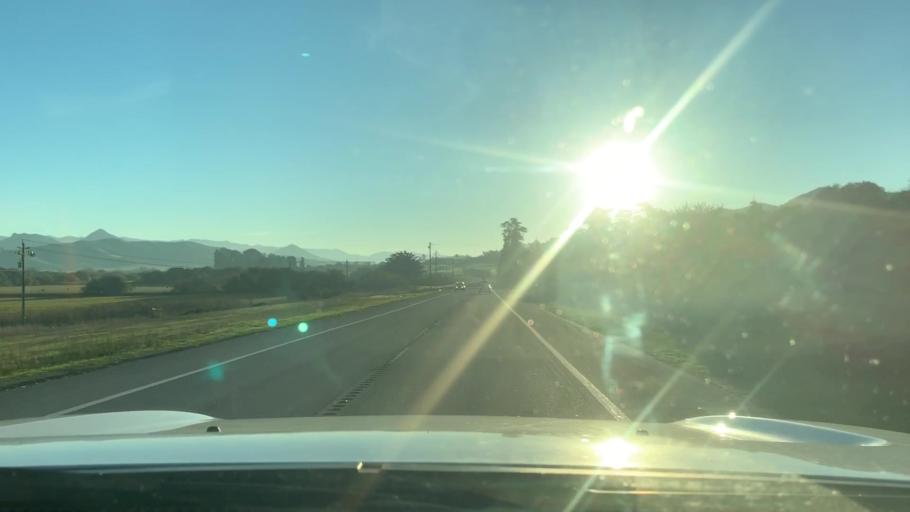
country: US
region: California
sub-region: San Luis Obispo County
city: Los Osos
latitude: 35.3012
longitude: -120.7921
